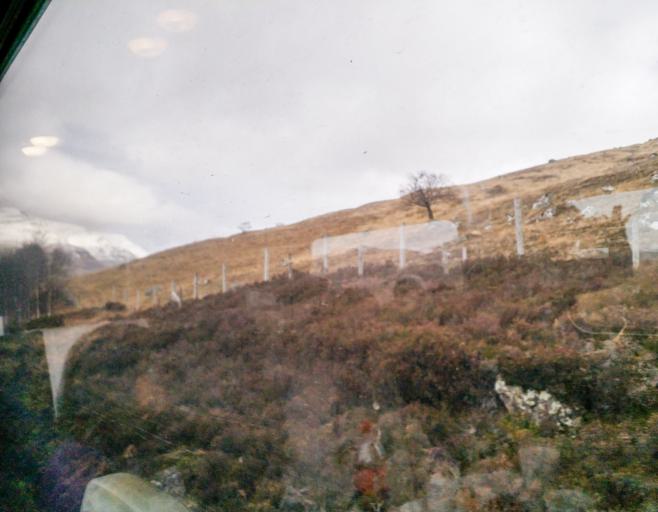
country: GB
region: Scotland
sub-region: Highland
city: Spean Bridge
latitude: 56.7785
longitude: -4.7321
